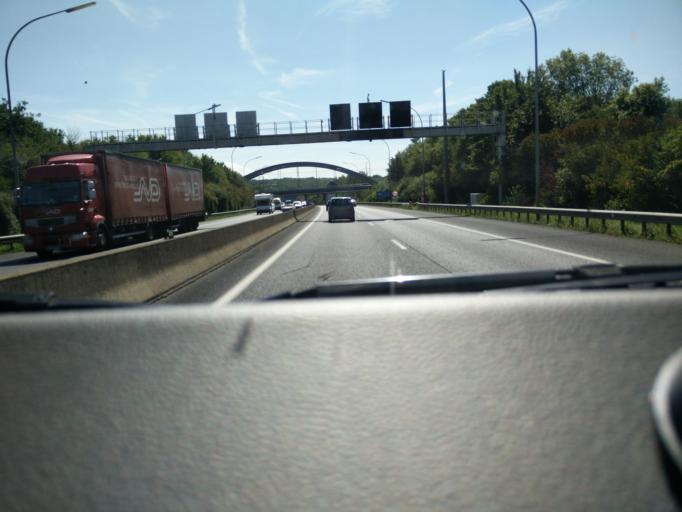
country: LU
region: Luxembourg
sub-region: Canton de Luxembourg
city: Strassen
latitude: 49.5926
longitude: 6.0816
